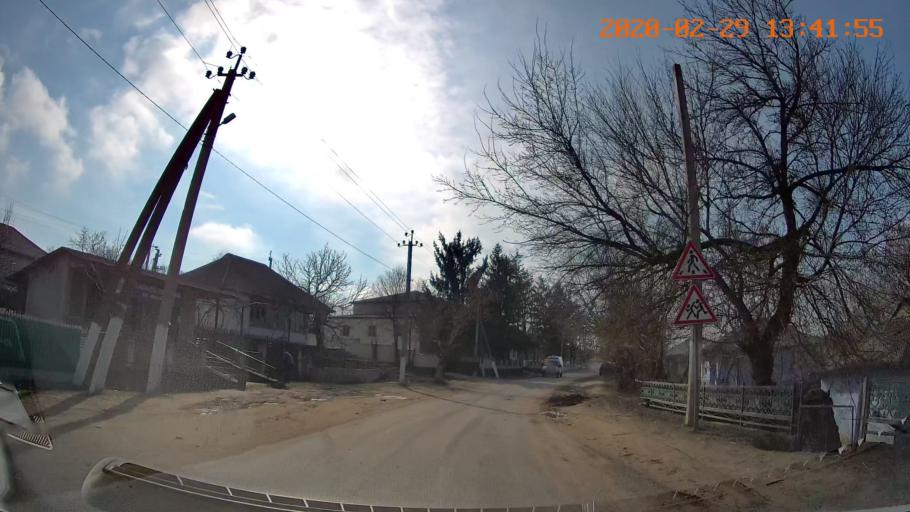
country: MD
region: Floresti
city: Leninskiy
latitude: 47.8432
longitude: 28.5544
